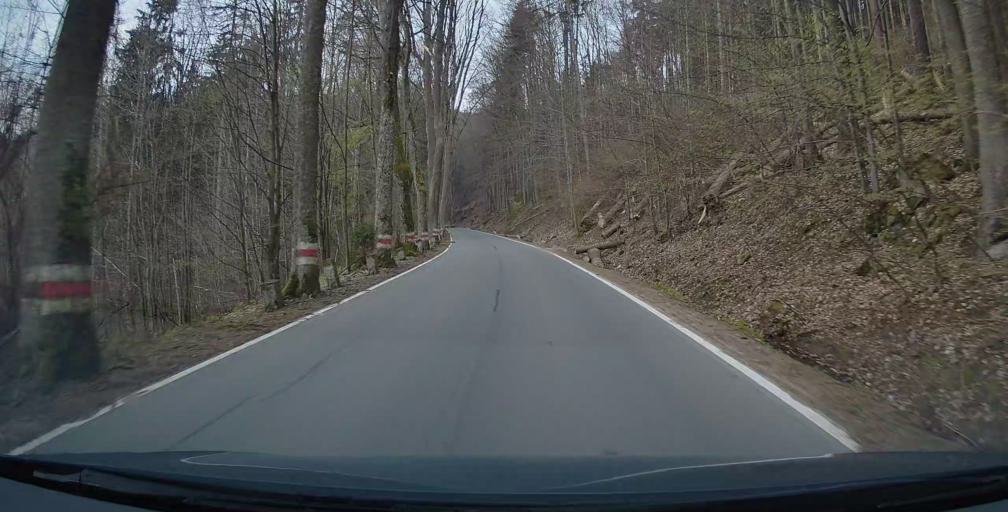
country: PL
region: Lower Silesian Voivodeship
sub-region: Powiat klodzki
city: Radkow
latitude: 50.4873
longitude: 16.3732
